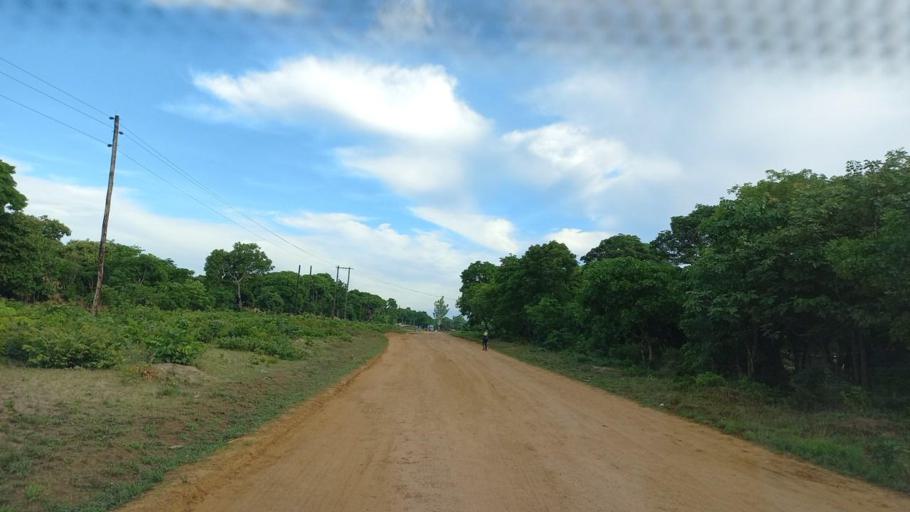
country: ZM
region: North-Western
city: Kabompo
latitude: -13.4048
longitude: 24.3116
